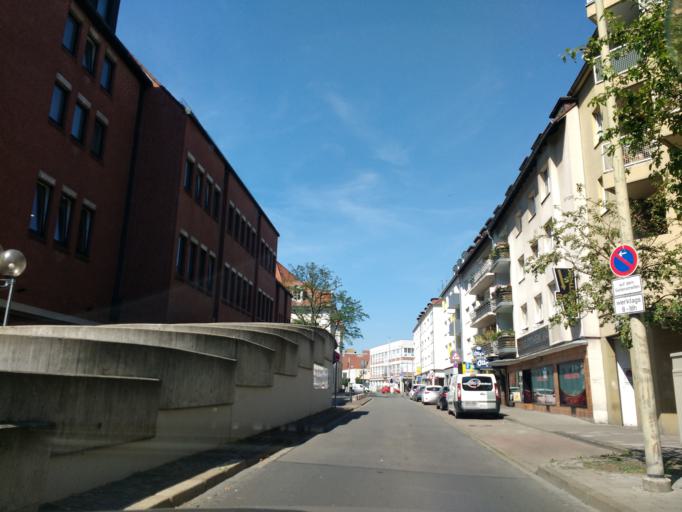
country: DE
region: Lower Saxony
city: Braunschweig
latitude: 52.2656
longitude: 10.5225
